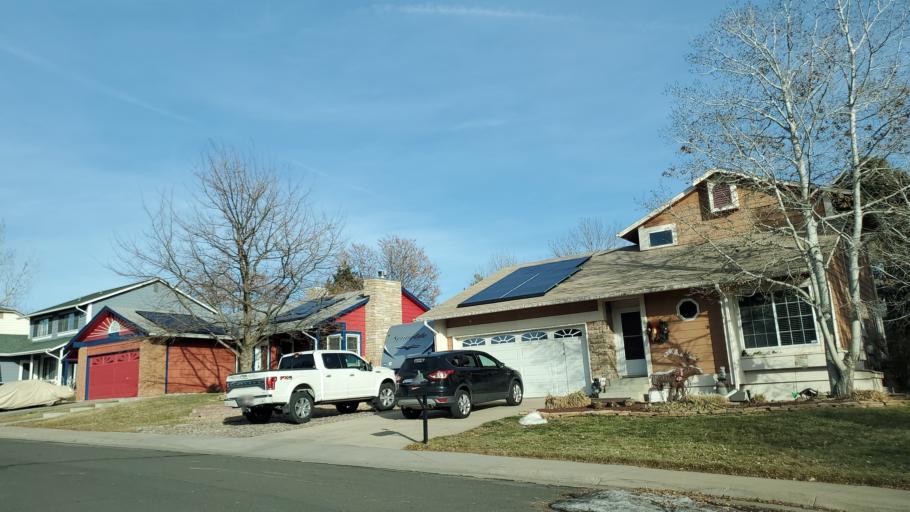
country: US
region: Colorado
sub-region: Adams County
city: Northglenn
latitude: 39.9052
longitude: -104.9539
